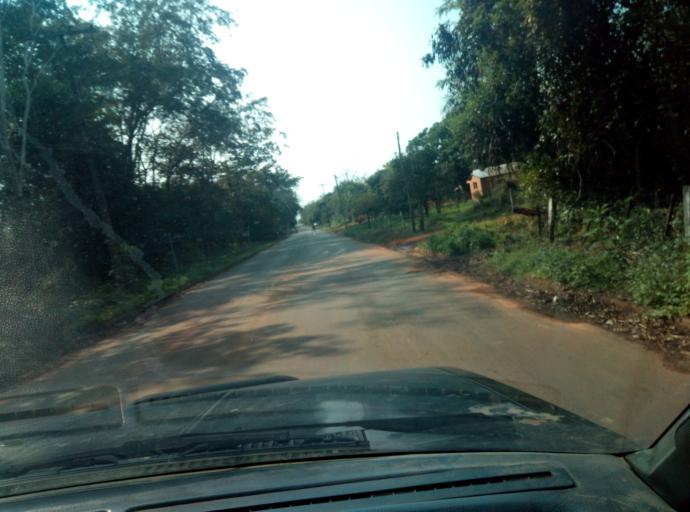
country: PY
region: Caaguazu
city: Carayao
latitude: -25.2104
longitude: -56.3006
